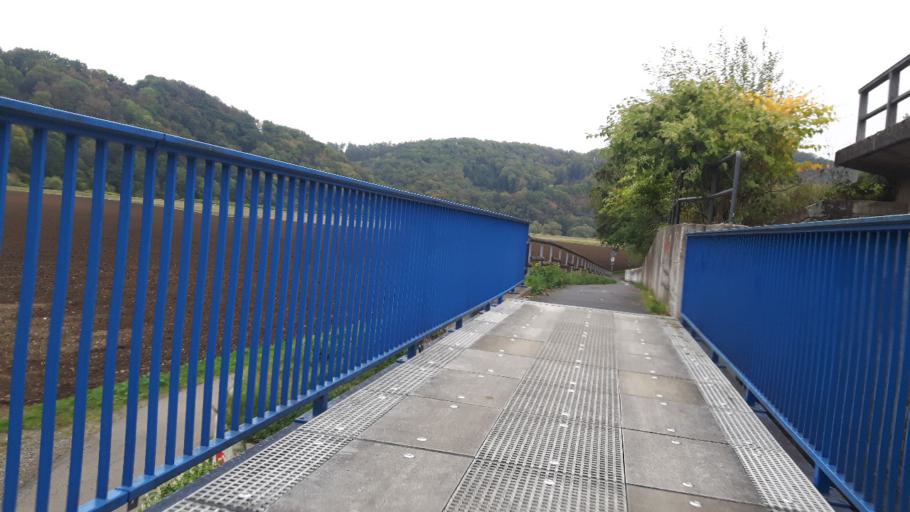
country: DE
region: North Rhine-Westphalia
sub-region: Regierungsbezirk Koln
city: Hennef
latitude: 50.7726
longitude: 7.3655
